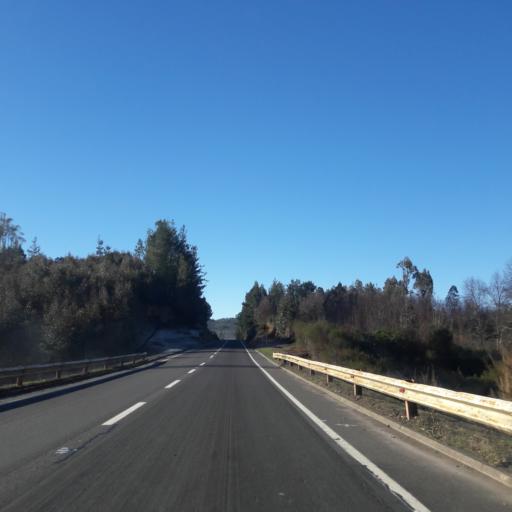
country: CL
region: Biobio
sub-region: Provincia de Biobio
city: La Laja
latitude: -37.2818
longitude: -72.9445
